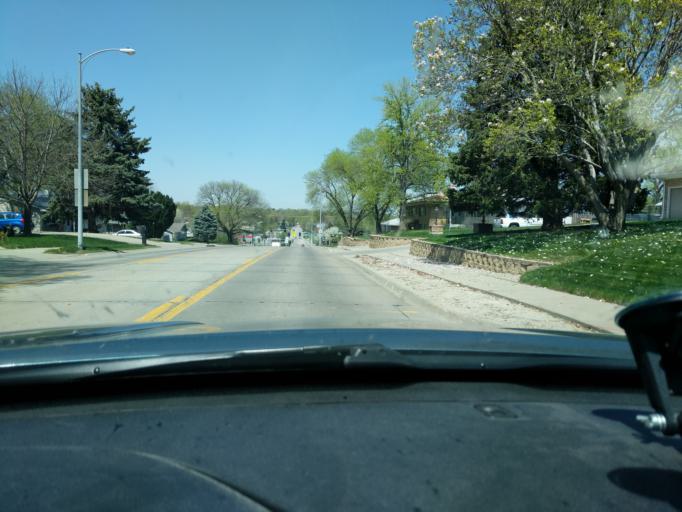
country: US
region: Nebraska
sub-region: Douglas County
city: Ralston
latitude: 41.2306
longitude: -96.0814
